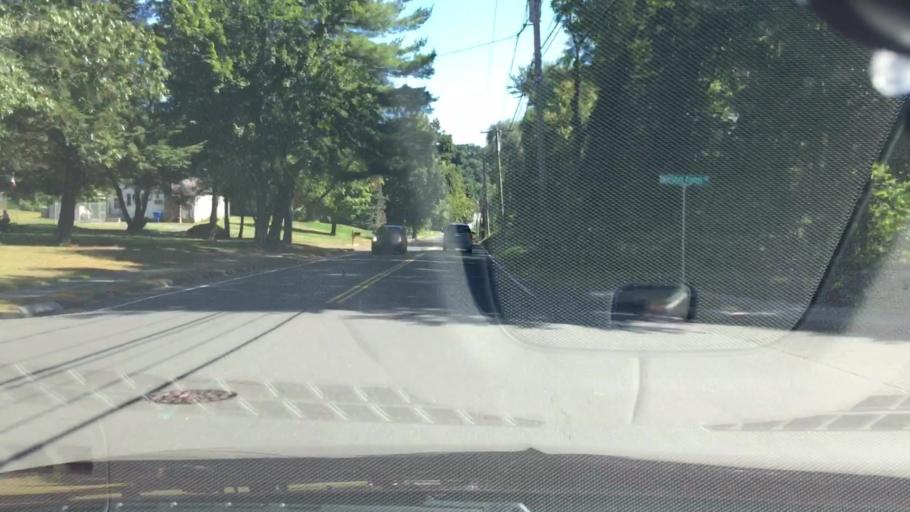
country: US
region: Connecticut
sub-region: Hartford County
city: Bristol
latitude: 41.7046
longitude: -72.9411
